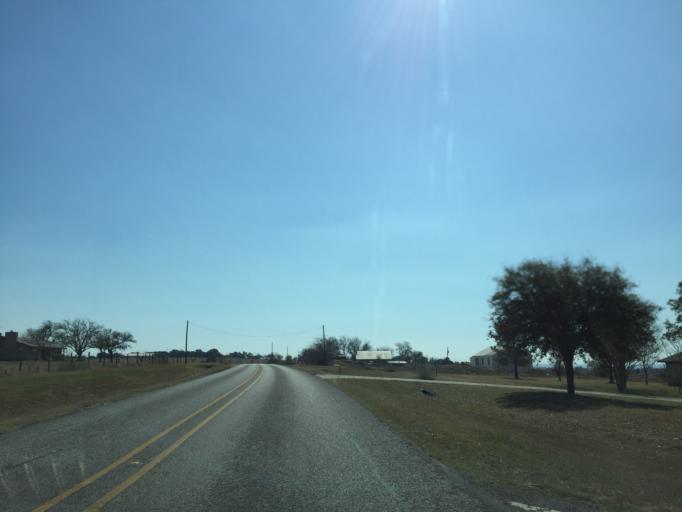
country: US
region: Texas
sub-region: Williamson County
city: Serenada
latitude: 30.7170
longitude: -97.5798
